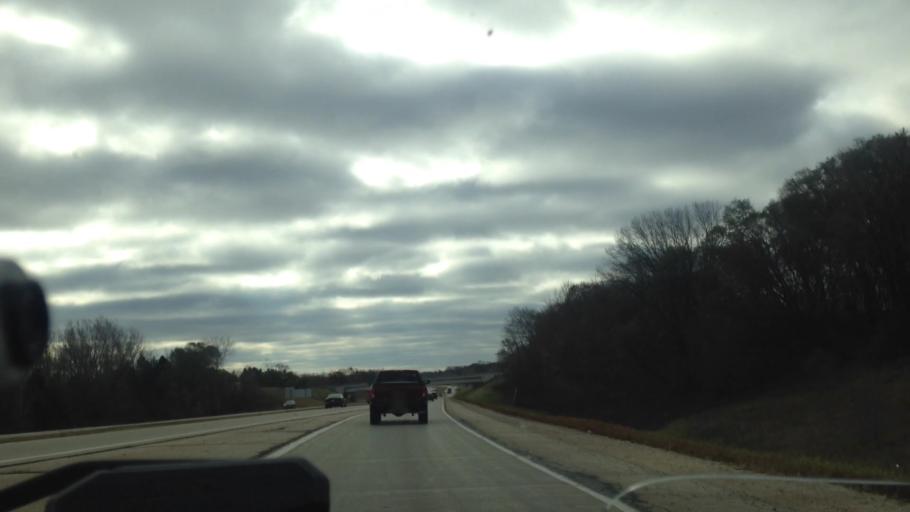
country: US
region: Wisconsin
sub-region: Washington County
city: West Bend
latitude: 43.4246
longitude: -88.2085
